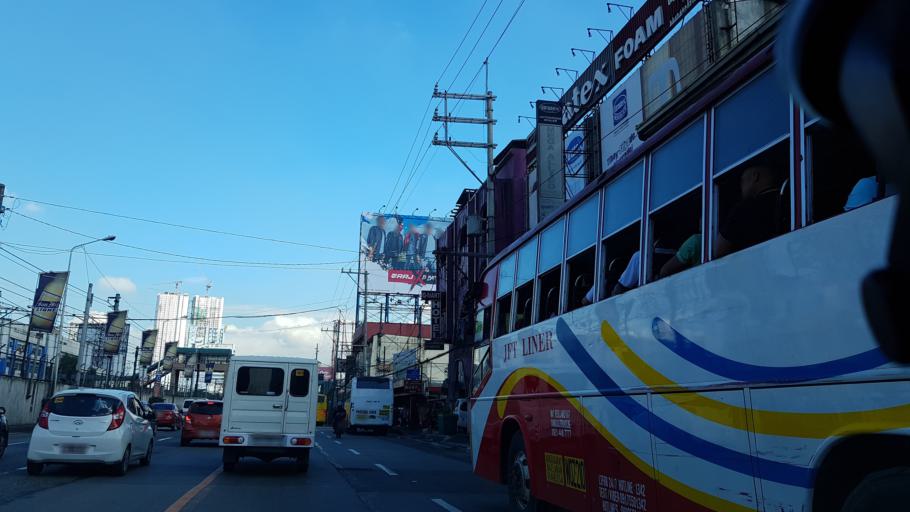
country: PH
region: Metro Manila
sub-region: Quezon City
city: Quezon City
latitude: 14.6264
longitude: 121.0480
